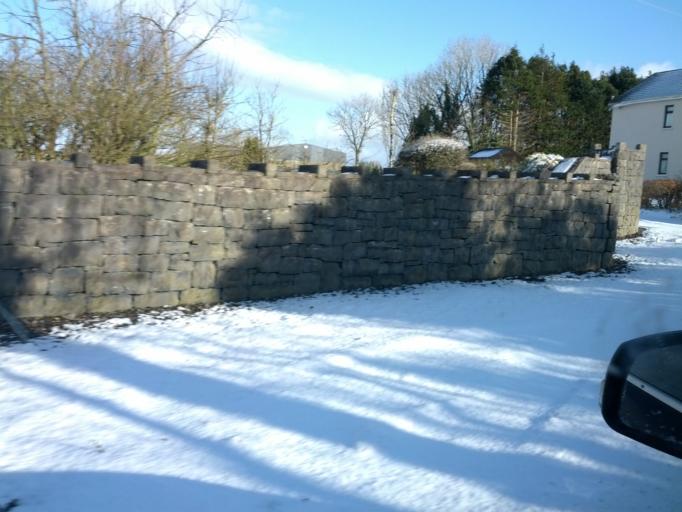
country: IE
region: Connaught
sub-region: County Galway
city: Athenry
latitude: 53.1867
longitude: -8.7863
